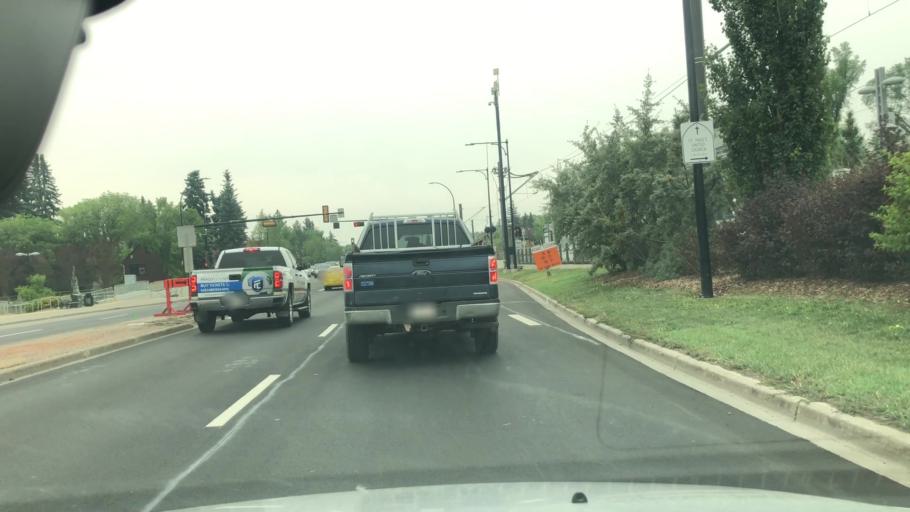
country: CA
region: Alberta
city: Edmonton
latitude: 53.5131
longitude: -113.5260
